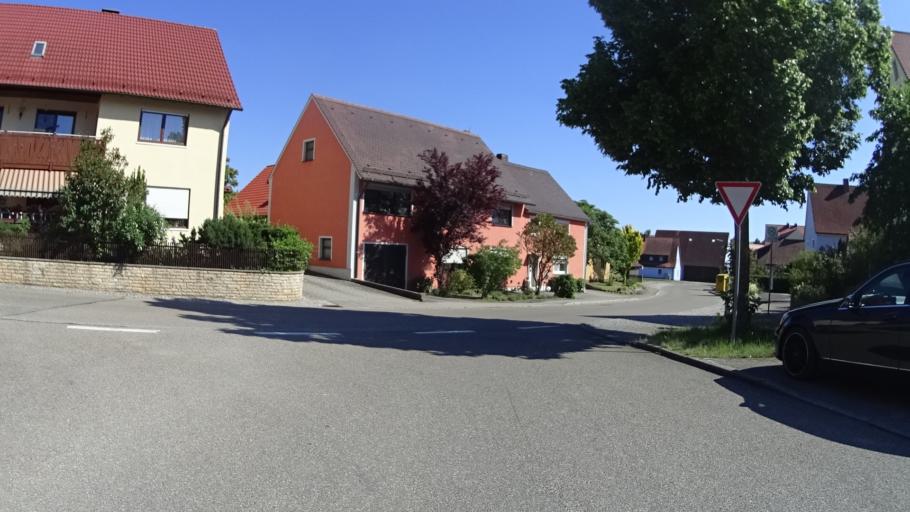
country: DE
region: Bavaria
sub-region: Regierungsbezirk Mittelfranken
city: Dombuhl
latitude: 49.2186
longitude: 10.3052
